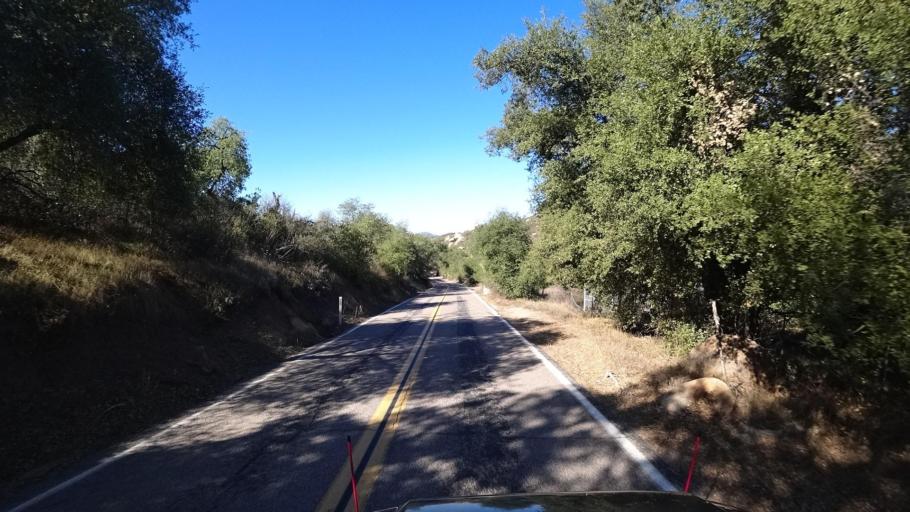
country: US
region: California
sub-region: San Diego County
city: Jamul
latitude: 32.7139
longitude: -116.7725
